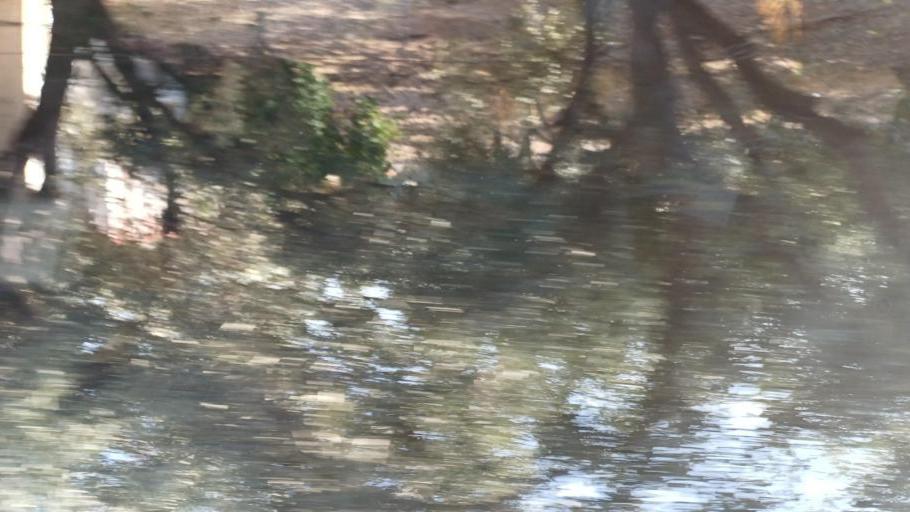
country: CY
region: Pafos
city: Pegeia
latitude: 34.8636
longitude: 32.3827
